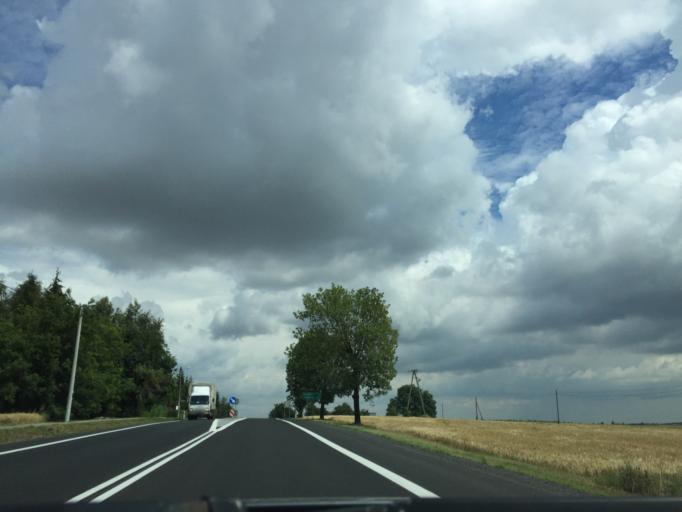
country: PL
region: Lesser Poland Voivodeship
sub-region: Powiat krakowski
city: Michalowice
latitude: 50.2064
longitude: 20.0164
